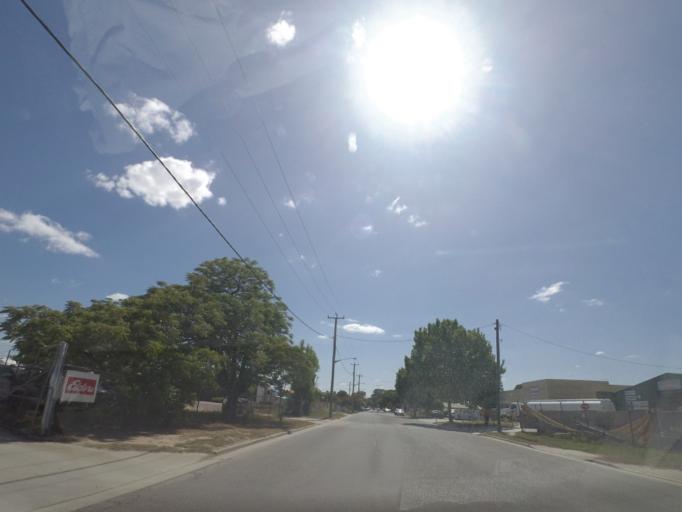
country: AU
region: New South Wales
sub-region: Albury Municipality
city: South Albury
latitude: -36.0935
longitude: 146.9176
